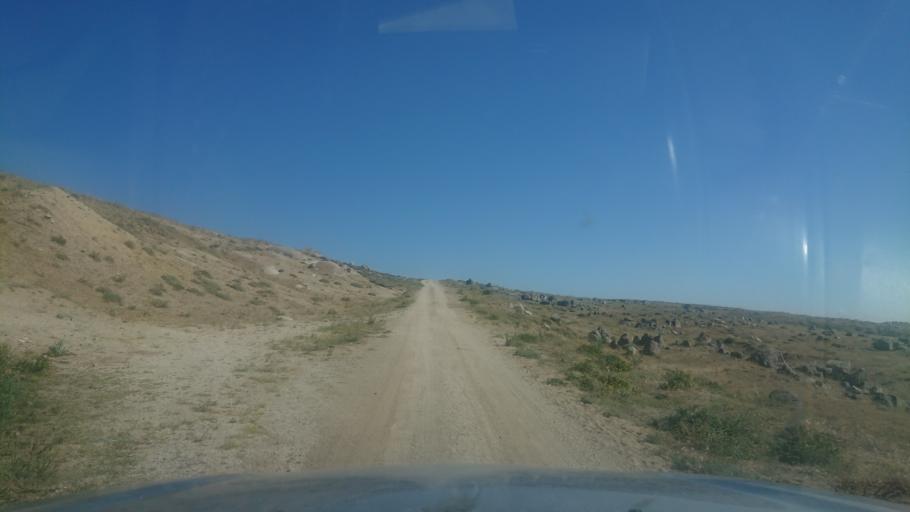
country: TR
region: Aksaray
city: Sariyahsi
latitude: 38.9212
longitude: 33.8524
